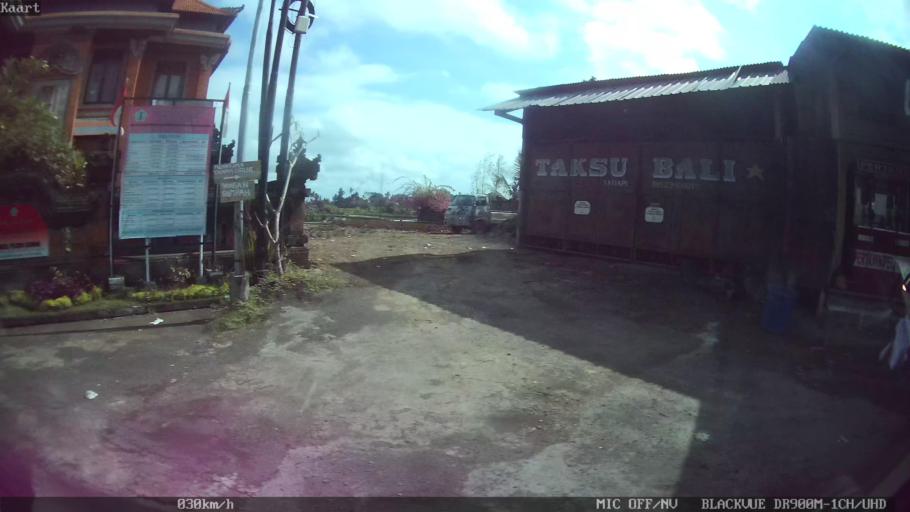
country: ID
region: Bali
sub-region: Kabupaten Gianyar
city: Ubud
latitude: -8.5113
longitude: 115.2844
